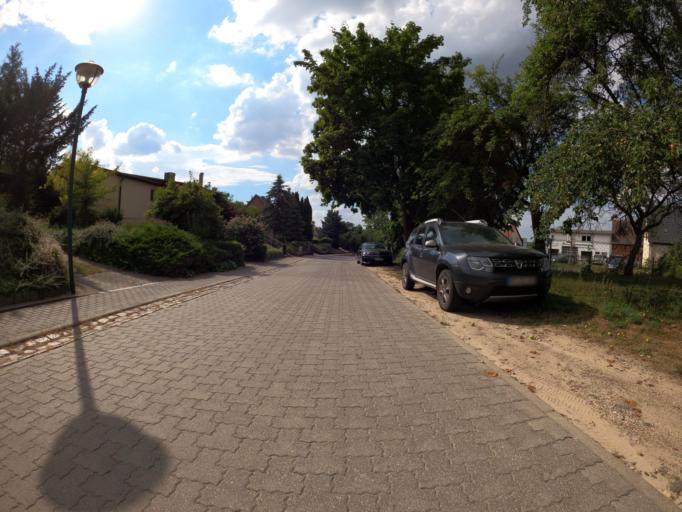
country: DE
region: Mecklenburg-Vorpommern
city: Woldegk
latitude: 53.3918
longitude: 13.5909
